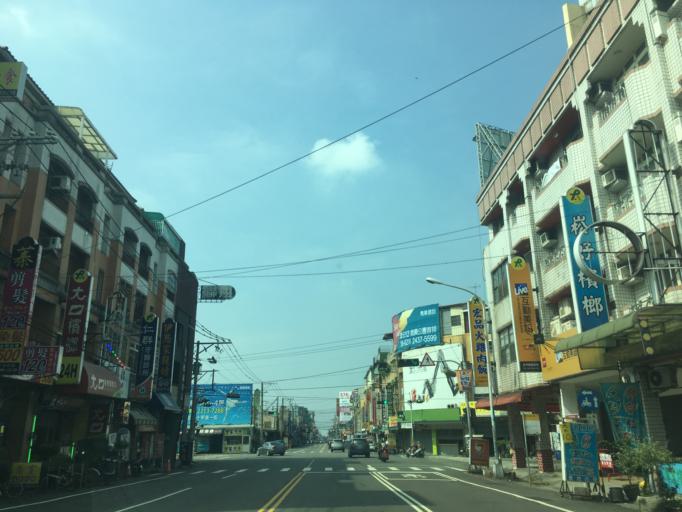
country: TW
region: Taiwan
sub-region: Taichung City
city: Taichung
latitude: 24.1518
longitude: 120.7111
